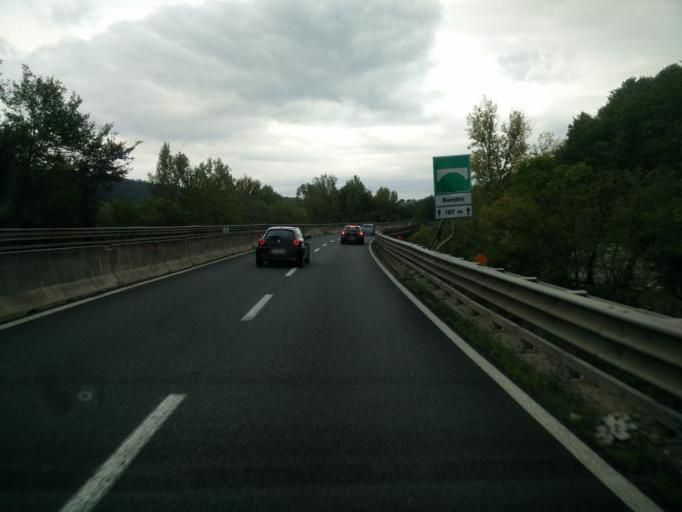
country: IT
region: Tuscany
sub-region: Province of Florence
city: Tavarnuzze
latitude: 43.6875
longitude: 11.2111
